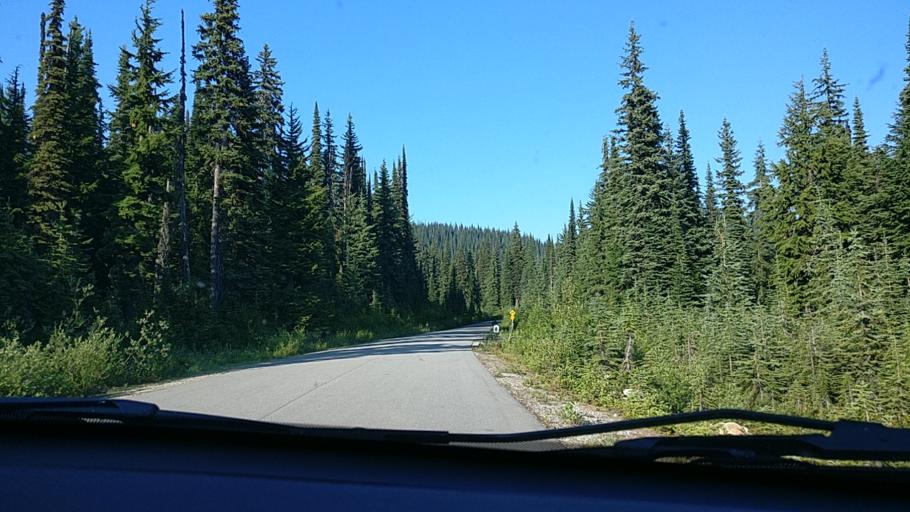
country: CA
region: British Columbia
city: Revelstoke
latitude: 51.0242
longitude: -118.1537
